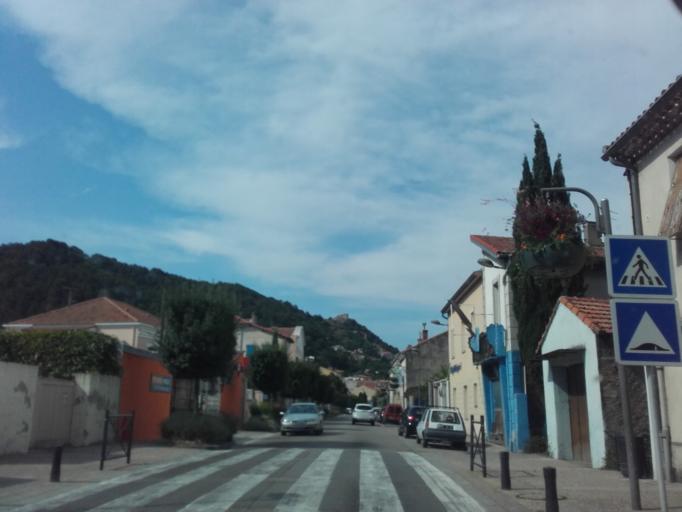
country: FR
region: Rhone-Alpes
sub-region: Departement de l'Ardeche
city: Le Teil
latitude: 44.5473
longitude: 4.6813
